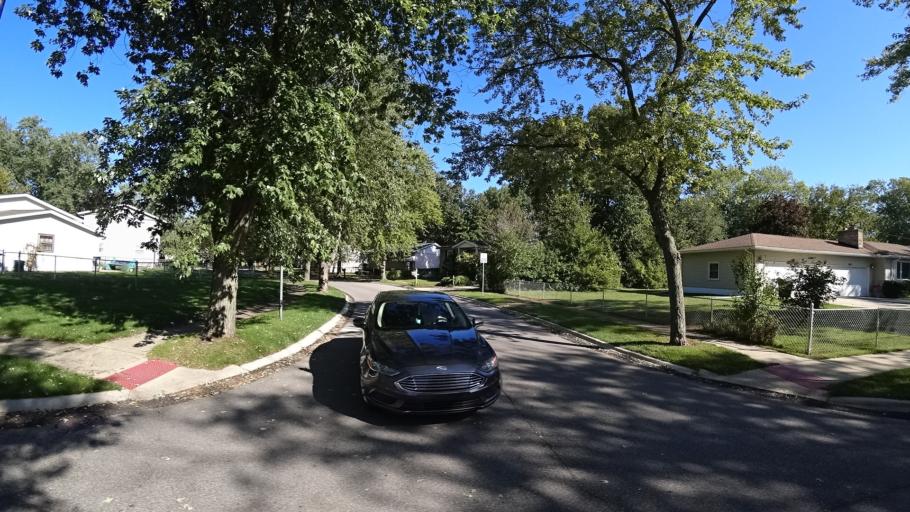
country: US
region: Indiana
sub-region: LaPorte County
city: Michigan City
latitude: 41.6894
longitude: -86.9057
